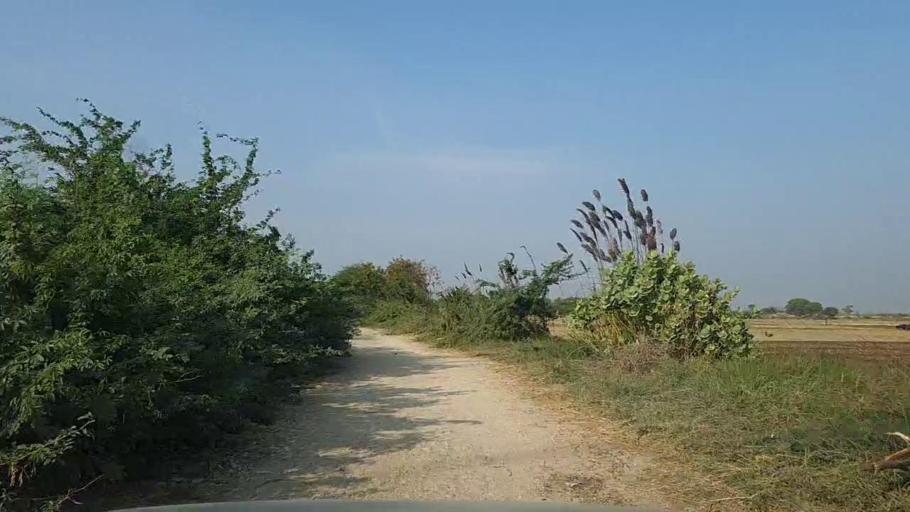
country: PK
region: Sindh
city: Mirpur Sakro
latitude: 24.5973
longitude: 67.6490
